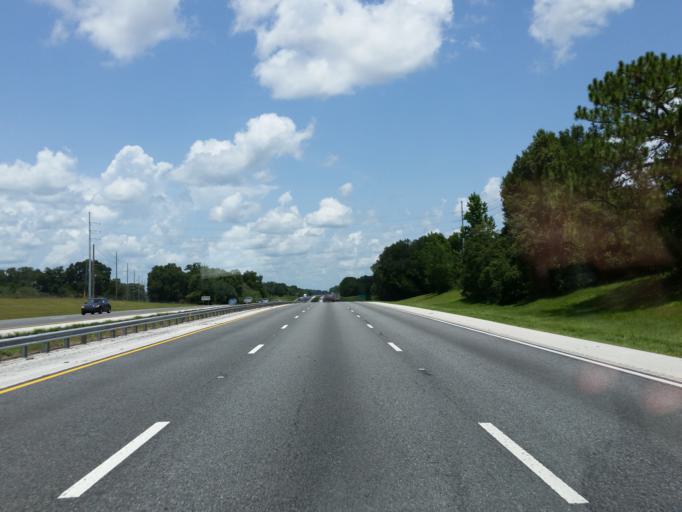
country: US
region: Florida
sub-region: Marion County
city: Ocala
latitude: 29.2779
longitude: -82.1969
